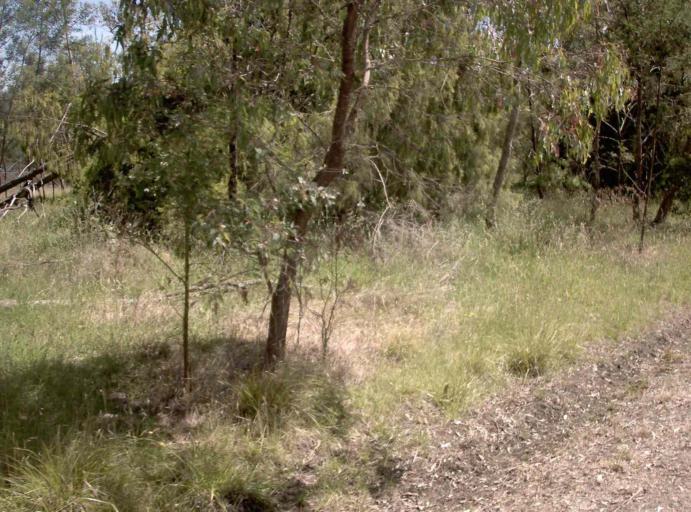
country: AU
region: Victoria
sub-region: East Gippsland
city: Lakes Entrance
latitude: -37.3347
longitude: 148.2323
